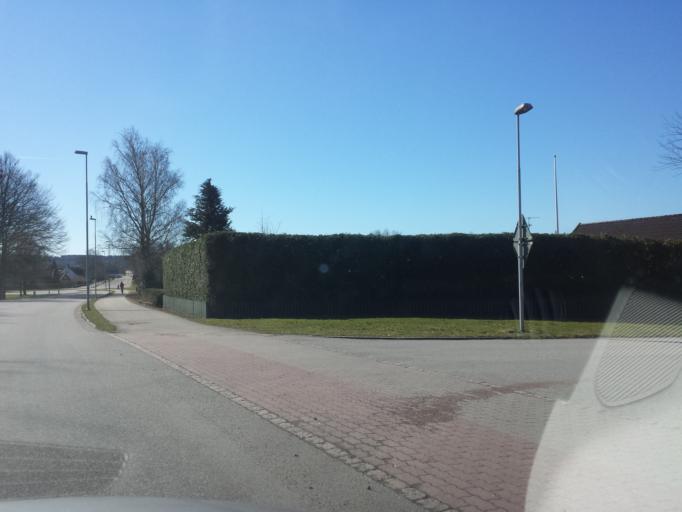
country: SE
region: Skane
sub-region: Sjobo Kommun
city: Sjoebo
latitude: 55.6428
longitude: 13.7047
